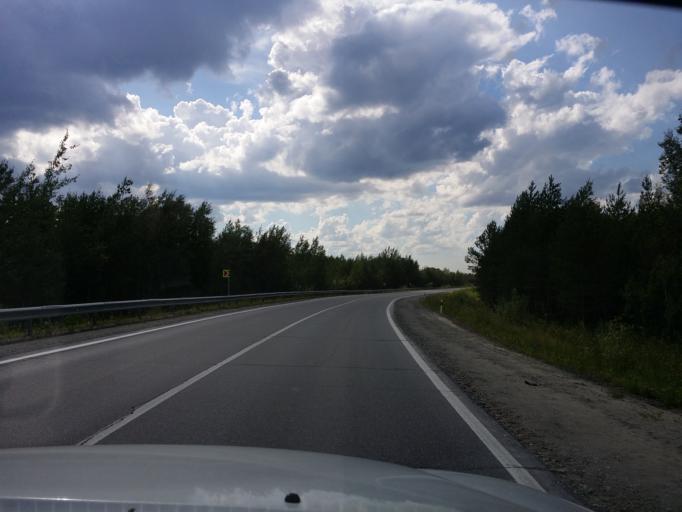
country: RU
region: Khanty-Mansiyskiy Avtonomnyy Okrug
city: Langepas
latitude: 61.1768
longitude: 75.5009
